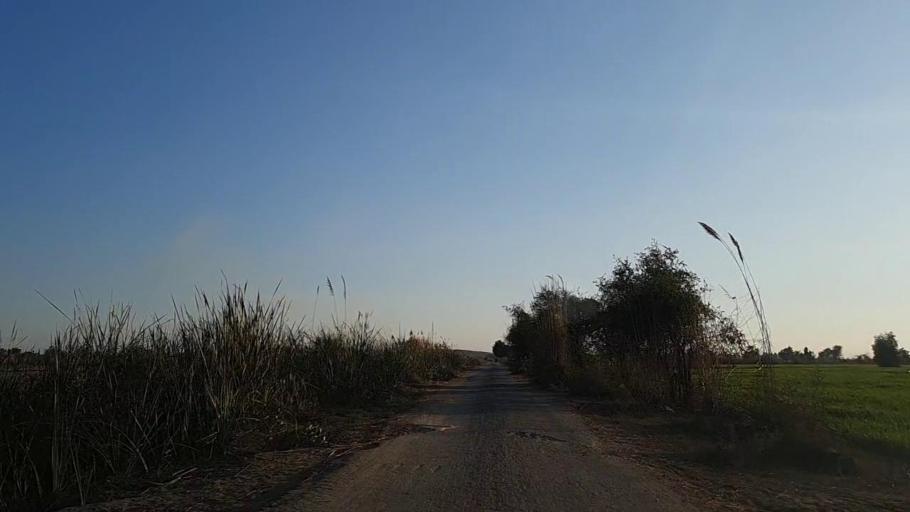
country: PK
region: Sindh
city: Khadro
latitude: 26.2696
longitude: 68.8099
